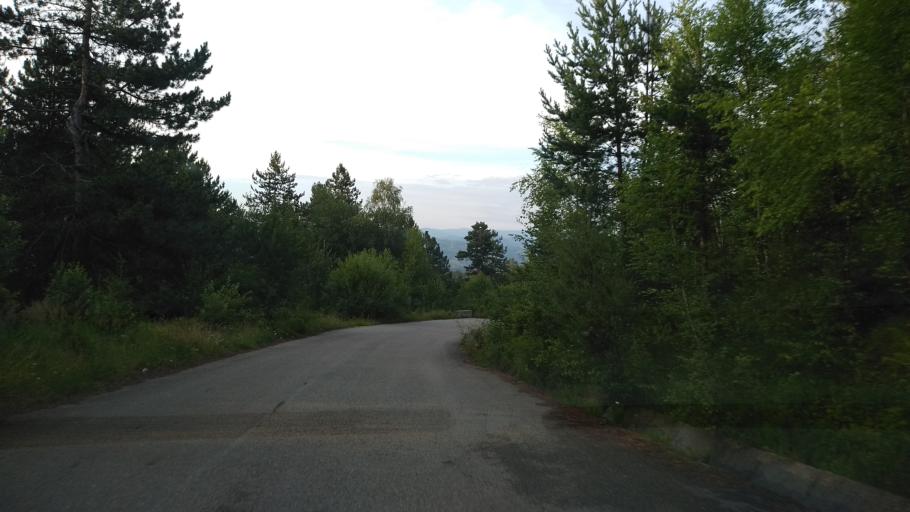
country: RO
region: Hunedoara
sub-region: Municipiul  Vulcan
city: Jiu-Paroseni
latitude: 45.3527
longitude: 23.2882
